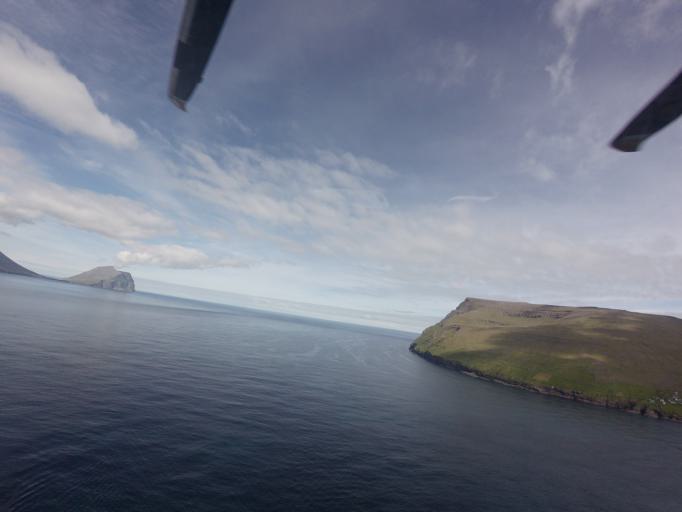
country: FO
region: Nordoyar
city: Klaksvik
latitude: 62.3076
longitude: -6.3330
